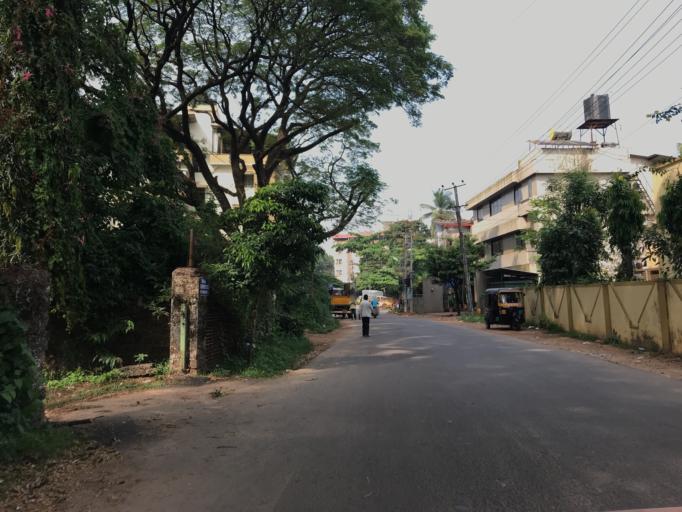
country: IN
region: Karnataka
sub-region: Dakshina Kannada
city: Ullal
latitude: 12.8473
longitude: 74.8525
